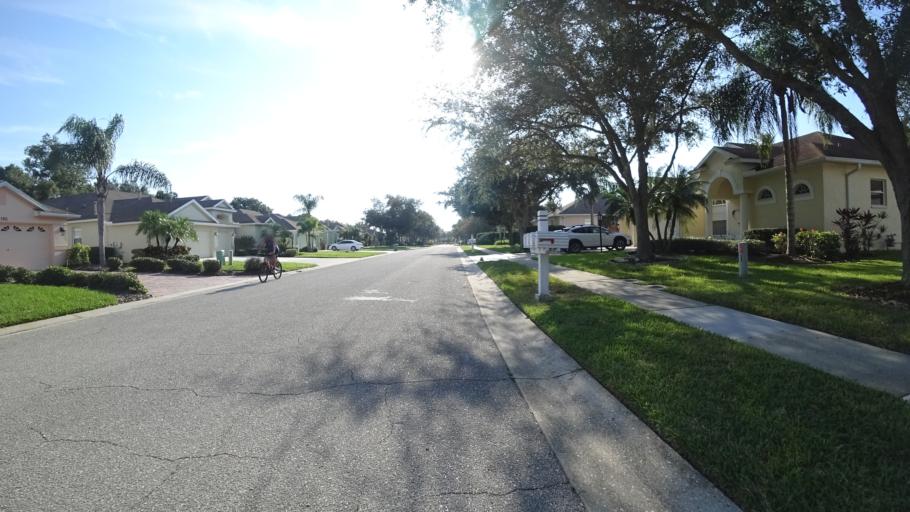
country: US
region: Florida
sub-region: Sarasota County
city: Desoto Lakes
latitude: 27.4240
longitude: -82.4963
